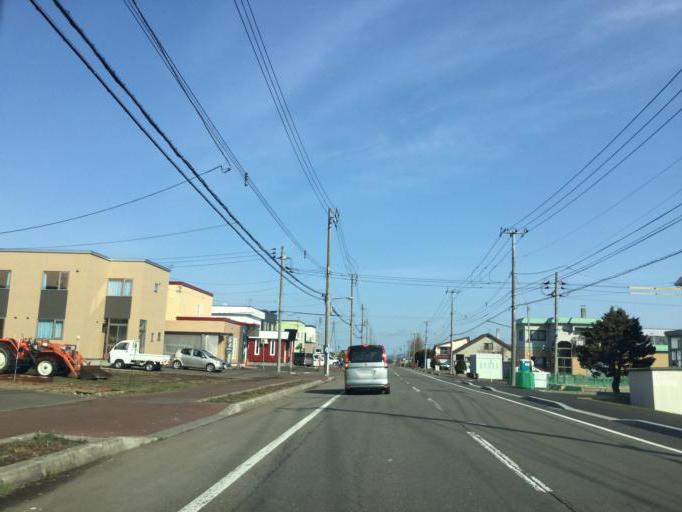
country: JP
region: Hokkaido
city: Ebetsu
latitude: 43.1496
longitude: 141.6495
